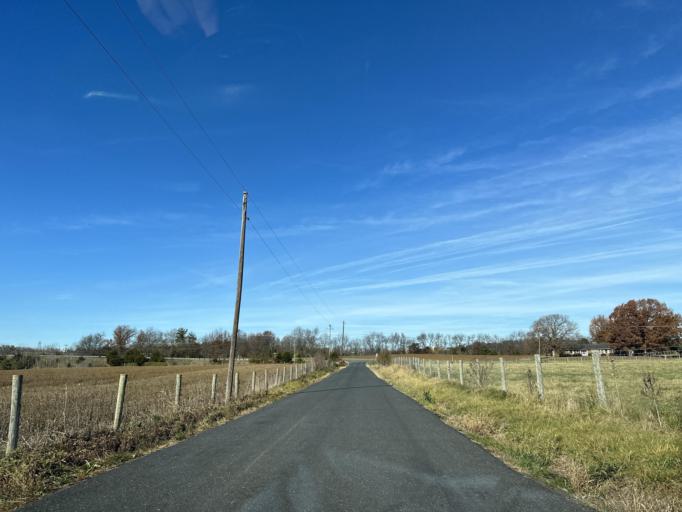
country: US
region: Virginia
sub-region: Augusta County
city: Weyers Cave
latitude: 38.2702
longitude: -78.9328
